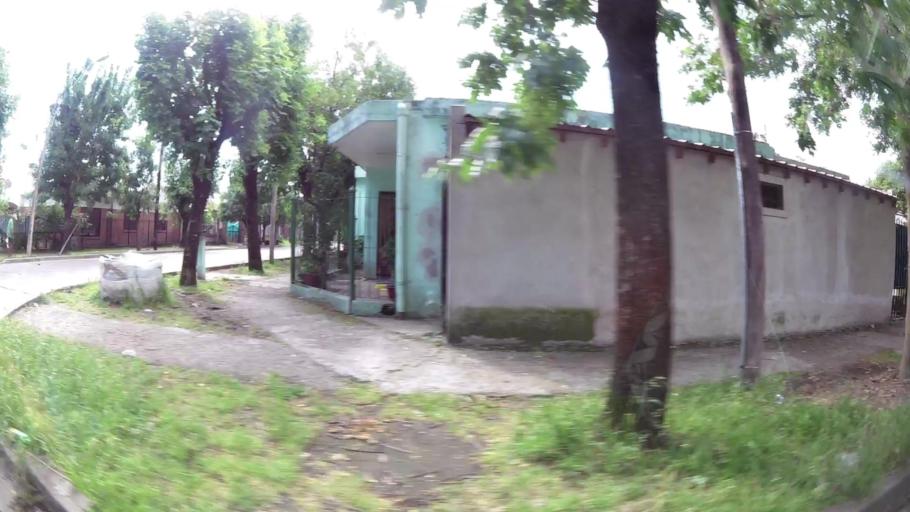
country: AR
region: Buenos Aires
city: Ituzaingo
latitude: -34.6482
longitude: -58.6808
